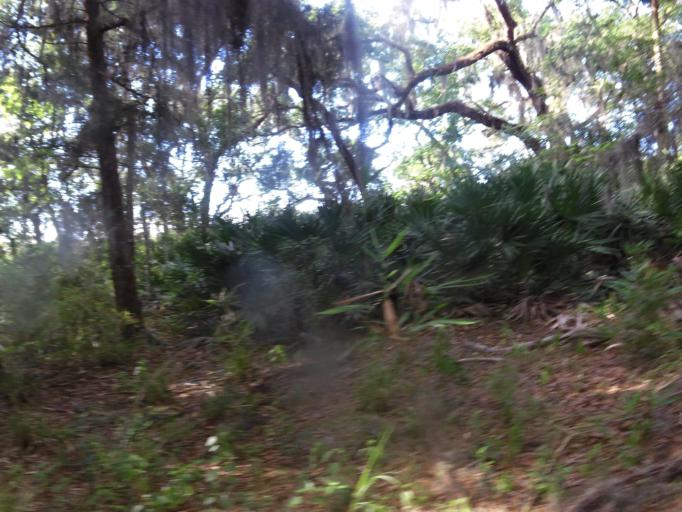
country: US
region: Florida
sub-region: Saint Johns County
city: Villano Beach
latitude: 30.0223
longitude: -81.3423
